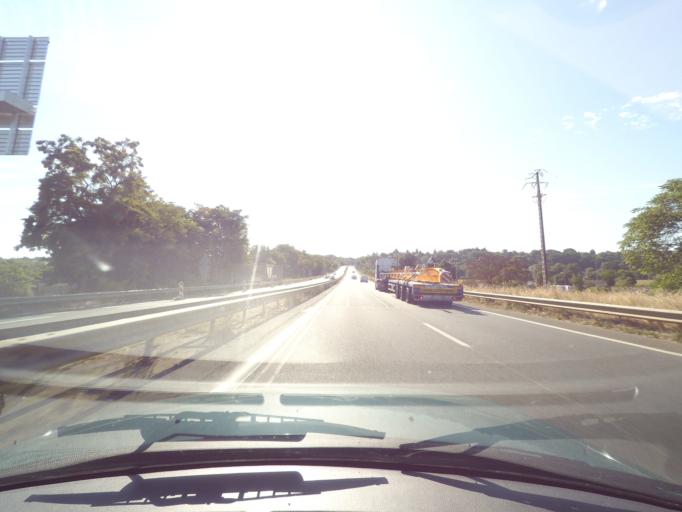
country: FR
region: Poitou-Charentes
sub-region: Departement de la Vienne
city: Chasseneuil-du-Poitou
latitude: 46.6192
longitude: 0.3546
